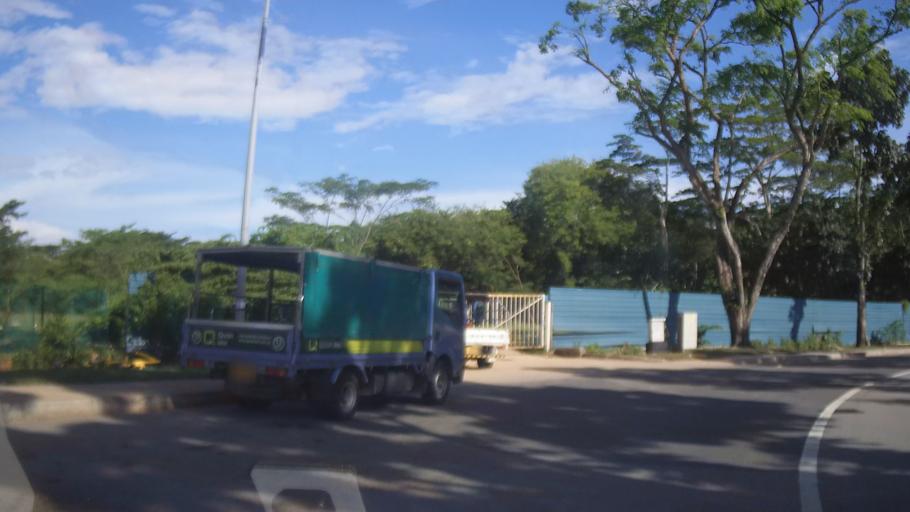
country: MY
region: Johor
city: Johor Bahru
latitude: 1.4341
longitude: 103.7585
